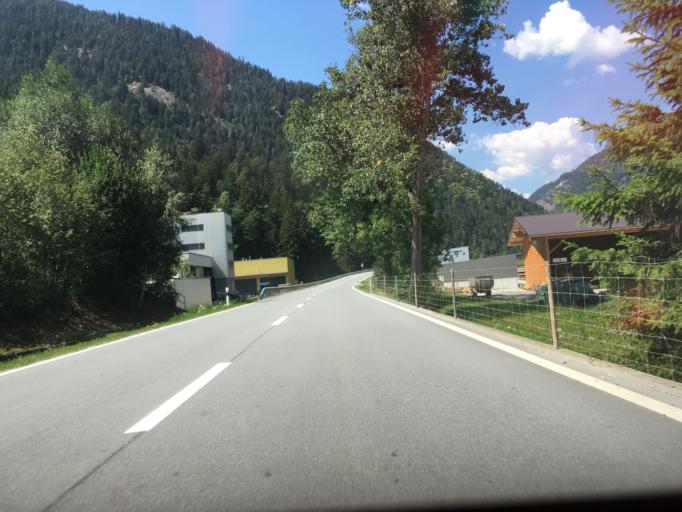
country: CH
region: Grisons
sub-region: Hinterrhein District
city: Cazis
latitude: 46.7592
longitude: 9.4197
